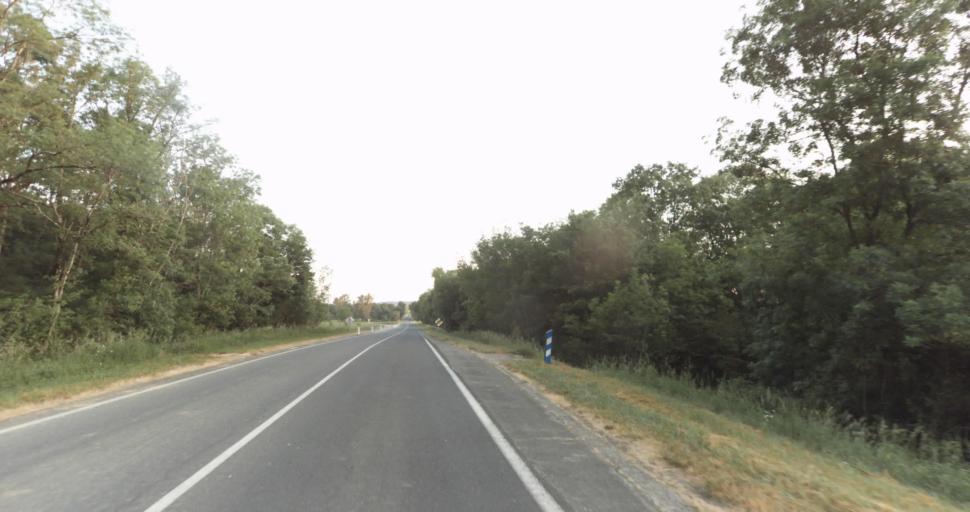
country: FR
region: Midi-Pyrenees
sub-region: Departement du Gers
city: Pujaudran
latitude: 43.6445
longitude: 1.1396
